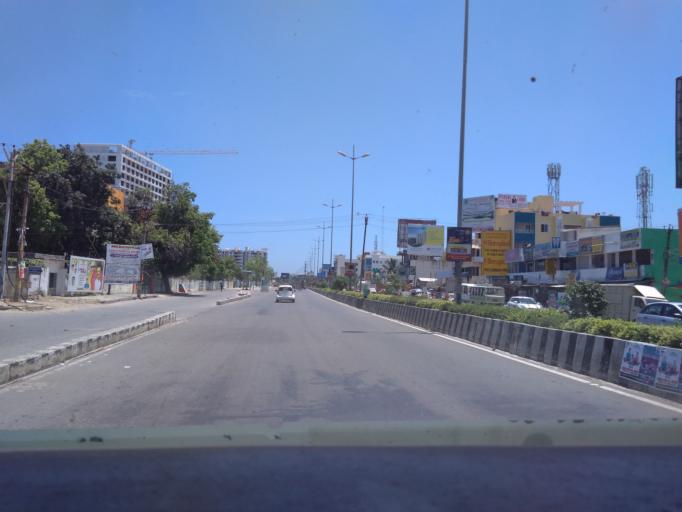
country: IN
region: Tamil Nadu
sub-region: Kancheepuram
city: Injambakkam
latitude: 12.8378
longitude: 80.2282
